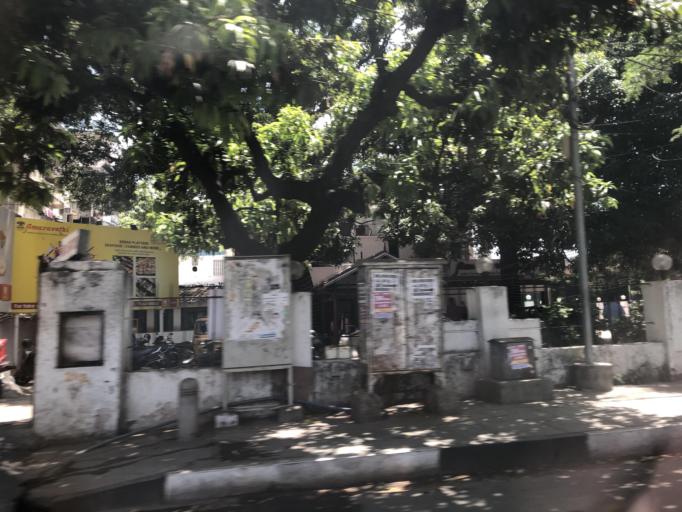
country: IN
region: Tamil Nadu
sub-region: Chennai
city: Chetput
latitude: 13.0447
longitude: 80.2597
